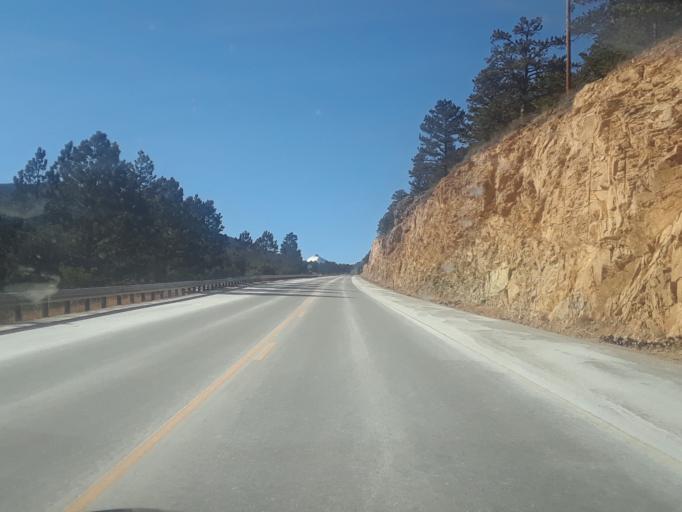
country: US
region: Colorado
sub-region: Larimer County
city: Estes Park
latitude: 40.1928
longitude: -105.5128
